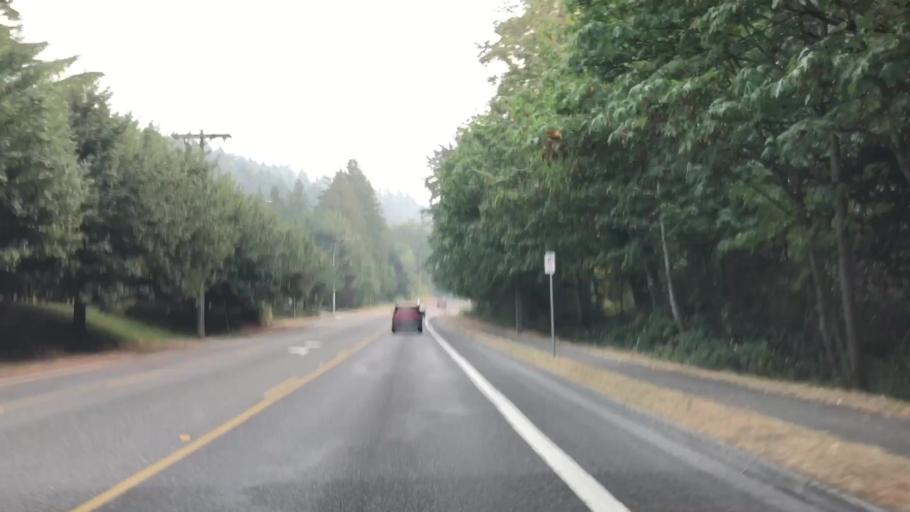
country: US
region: Washington
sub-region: Snohomish County
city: Brier
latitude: 47.7830
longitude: -122.2902
